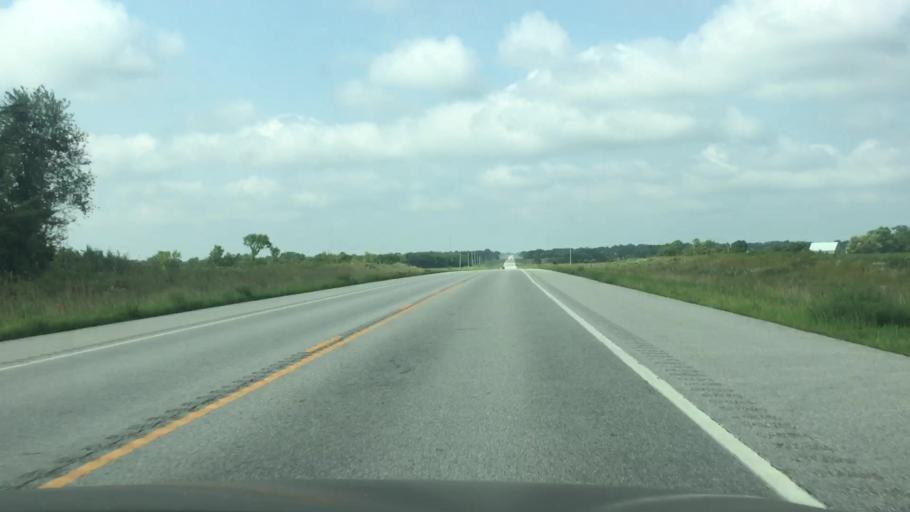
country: US
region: Kansas
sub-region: Miami County
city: Osawatomie
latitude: 38.4307
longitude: -95.0150
